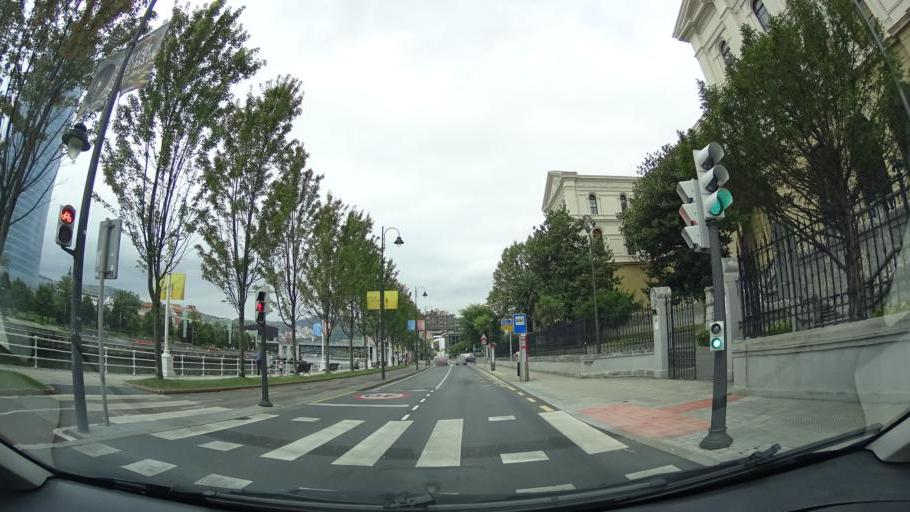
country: ES
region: Basque Country
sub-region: Bizkaia
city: Bilbao
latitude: 43.2702
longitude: -2.9374
